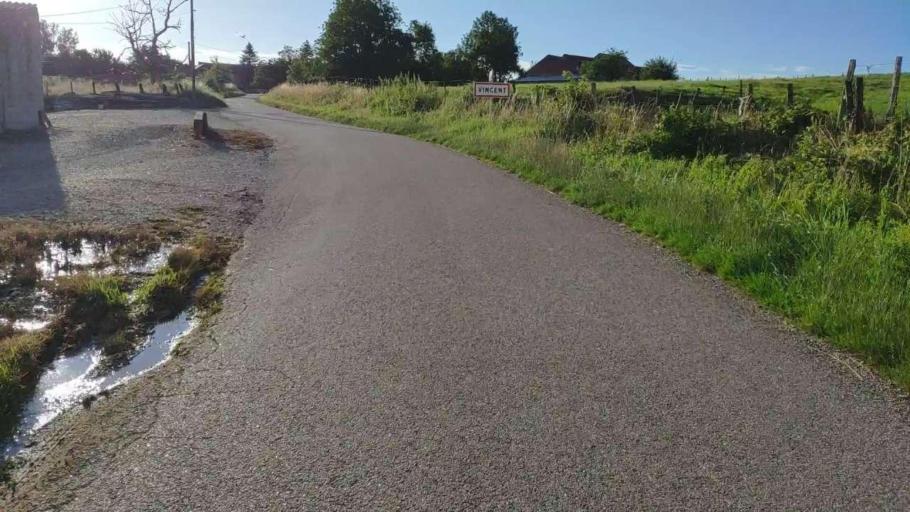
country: FR
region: Franche-Comte
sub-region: Departement du Jura
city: Bletterans
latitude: 46.7792
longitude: 5.4950
